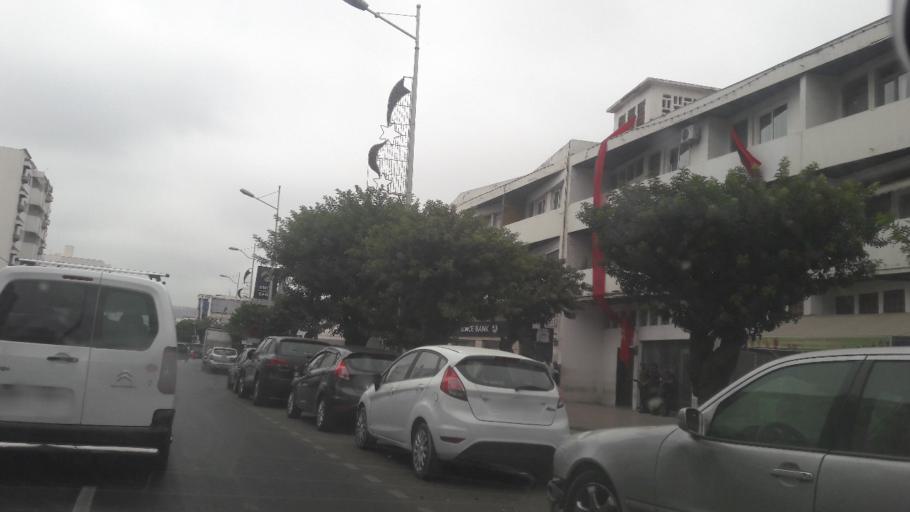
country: MA
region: Souss-Massa-Draa
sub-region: Agadir-Ida-ou-Tnan
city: Agadir
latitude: 30.4106
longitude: -9.5900
